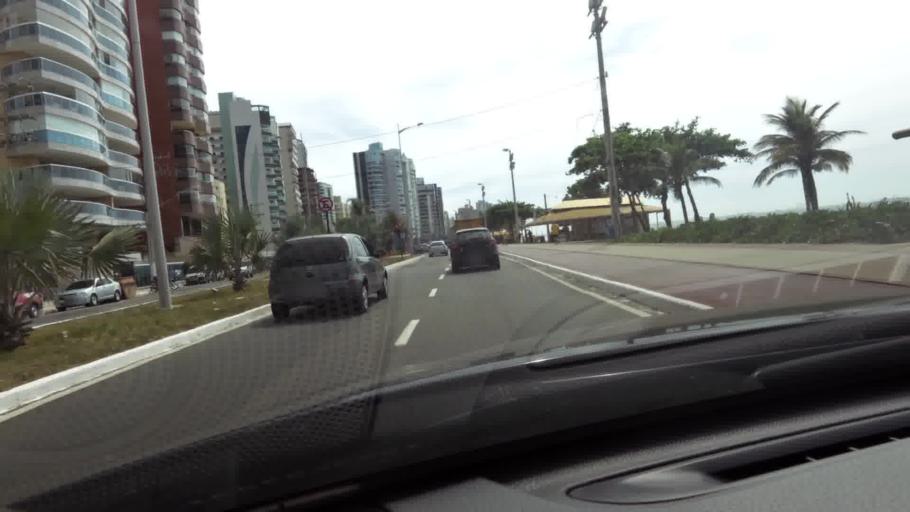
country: BR
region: Espirito Santo
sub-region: Vila Velha
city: Vila Velha
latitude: -20.3607
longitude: -40.2951
